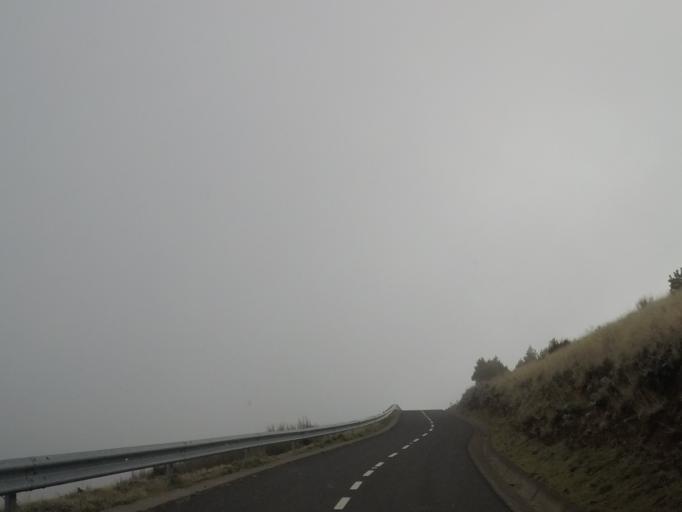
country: PT
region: Madeira
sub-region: Camara de Lobos
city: Curral das Freiras
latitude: 32.7231
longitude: -16.9418
